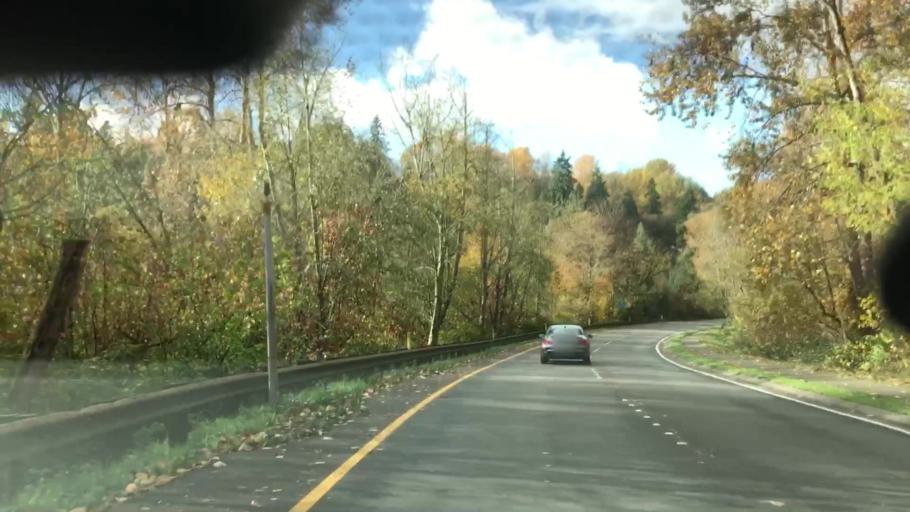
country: US
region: Washington
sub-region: King County
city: Eastgate
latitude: 47.5975
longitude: -122.1641
